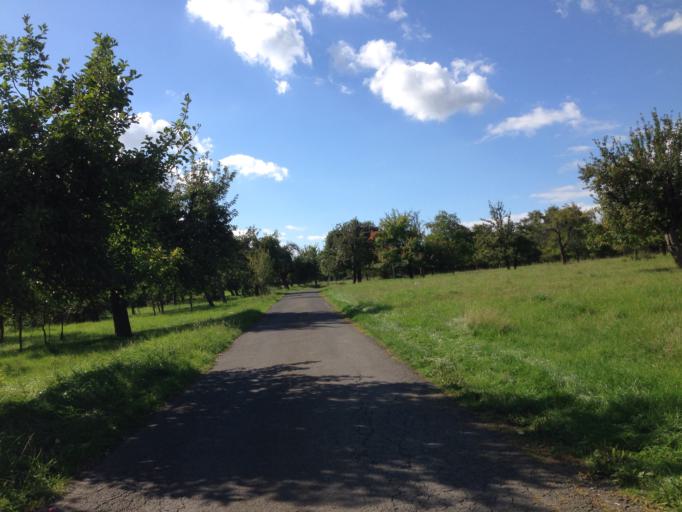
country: DE
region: Hesse
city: Lollar
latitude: 50.6166
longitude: 8.7080
